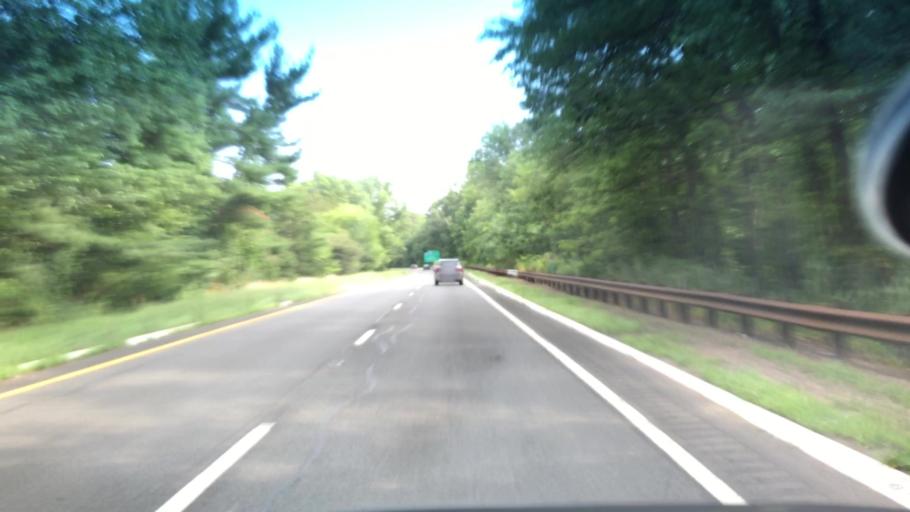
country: US
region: New York
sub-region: Rockland County
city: Bardonia
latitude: 41.1147
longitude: -74.0028
